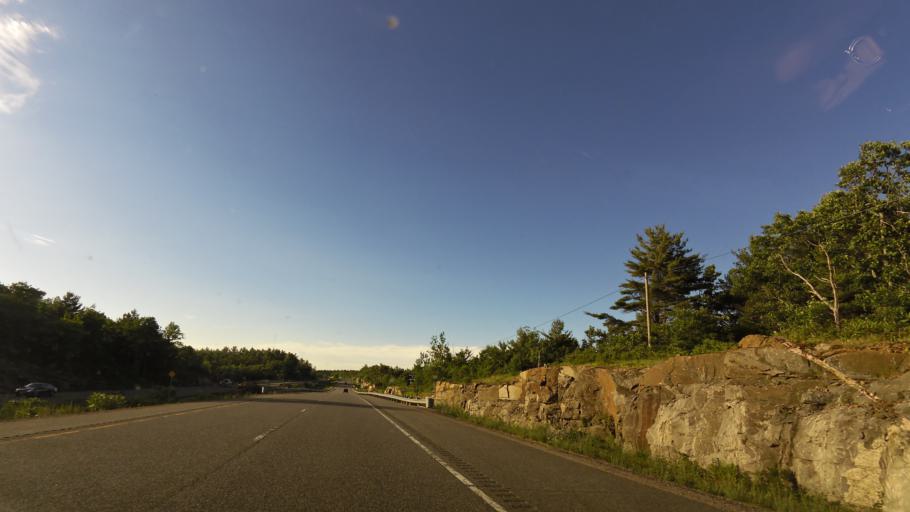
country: CA
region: Ontario
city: Midland
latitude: 44.9273
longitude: -79.7748
